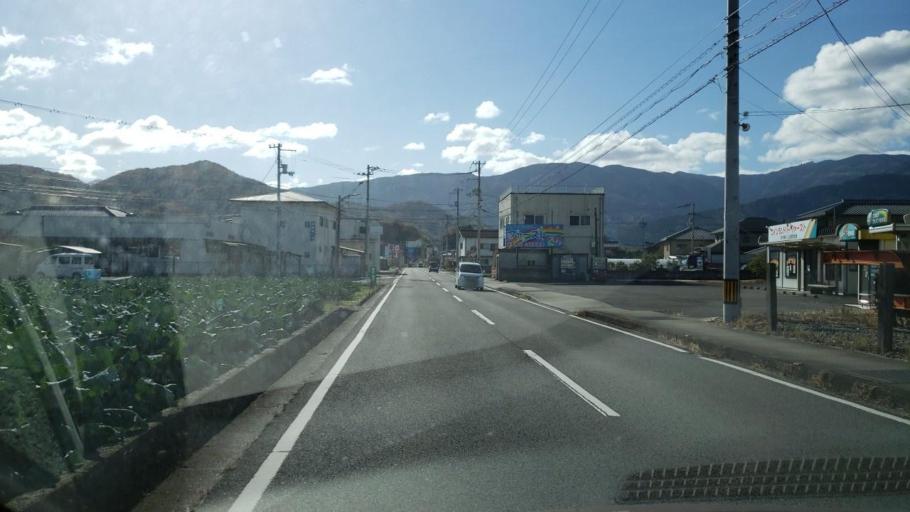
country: JP
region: Tokushima
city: Wakimachi
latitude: 34.0617
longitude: 134.2381
